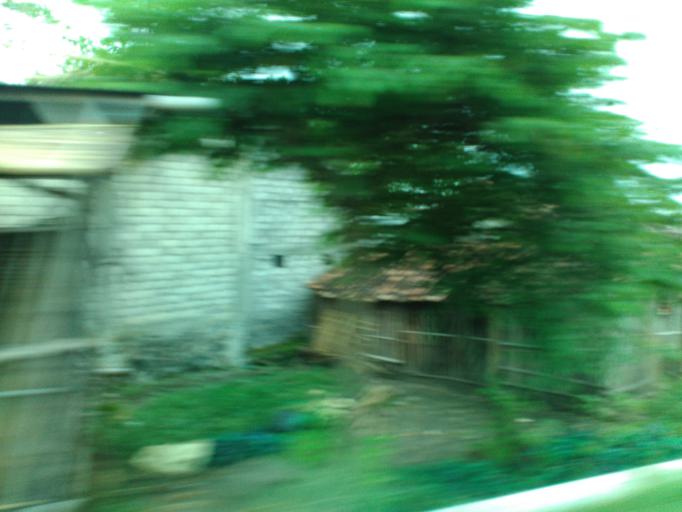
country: ID
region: Central Java
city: Gatak
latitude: -7.5898
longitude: 110.7065
